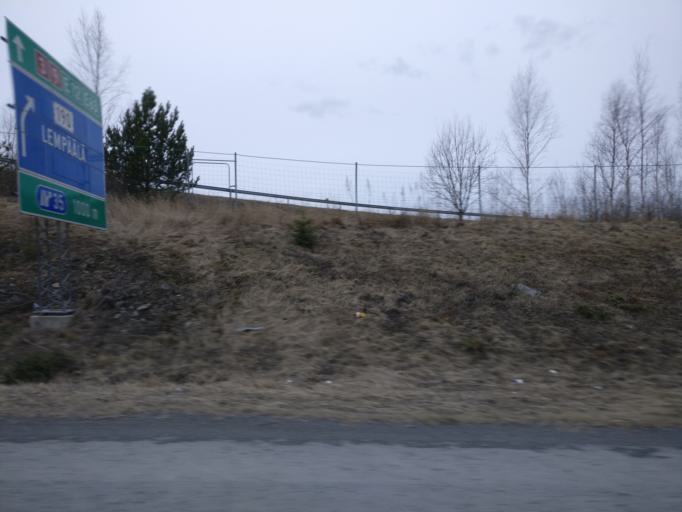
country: FI
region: Pirkanmaa
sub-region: Tampere
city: Lempaeaelae
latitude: 61.3451
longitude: 23.7892
